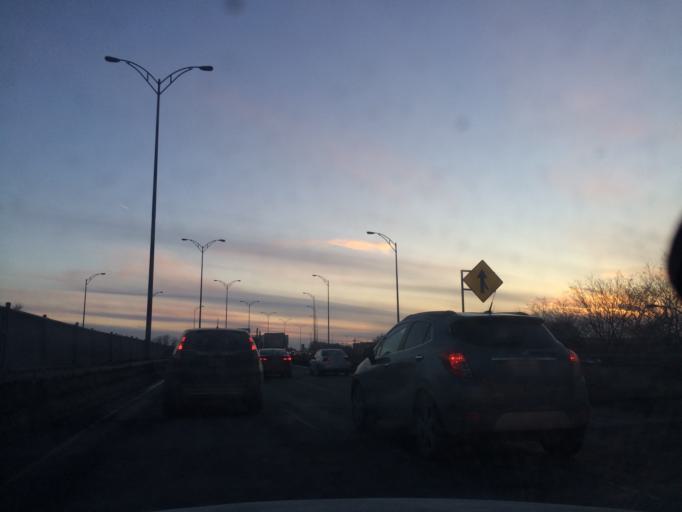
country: CA
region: Quebec
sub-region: Montreal
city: Saint-Leonard
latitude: 45.5613
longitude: -73.6078
